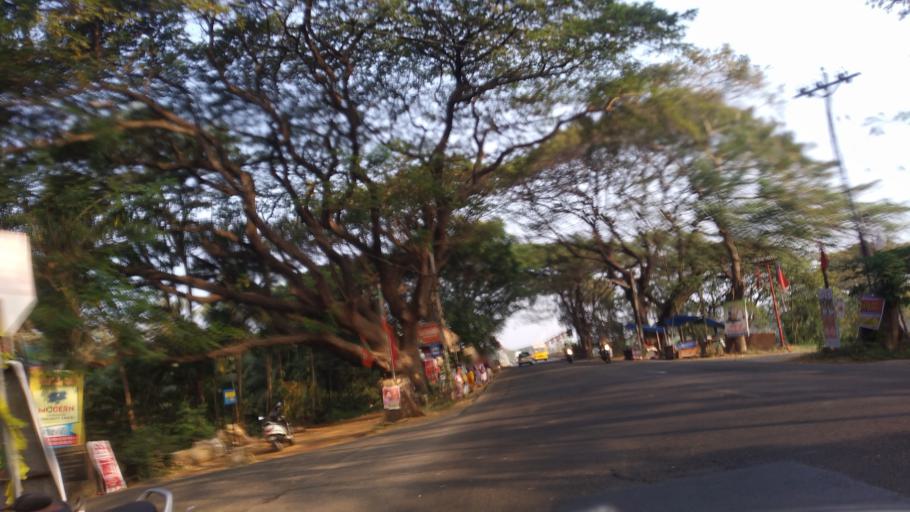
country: IN
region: Kerala
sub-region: Thrissur District
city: Kodungallur
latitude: 10.1972
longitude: 76.2008
